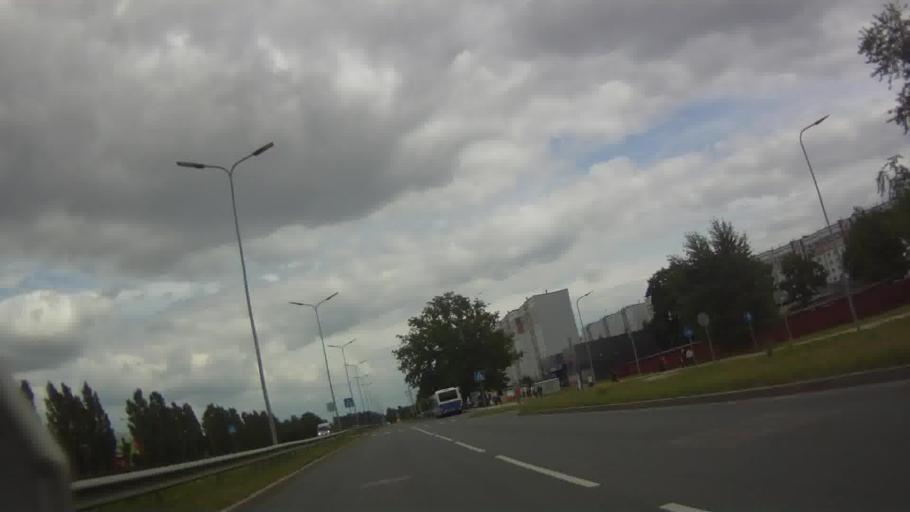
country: LV
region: Stopini
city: Ulbroka
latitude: 56.9445
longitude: 24.2206
